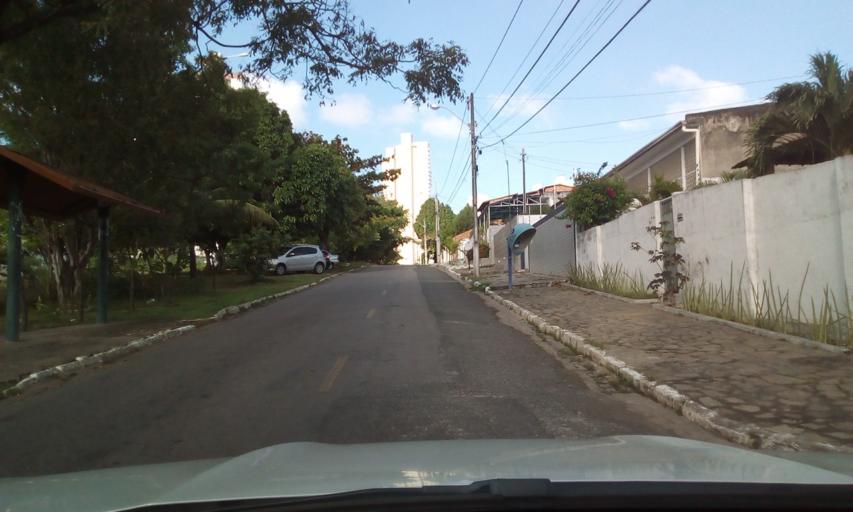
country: BR
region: Paraiba
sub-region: Joao Pessoa
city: Joao Pessoa
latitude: -7.1340
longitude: -34.8331
